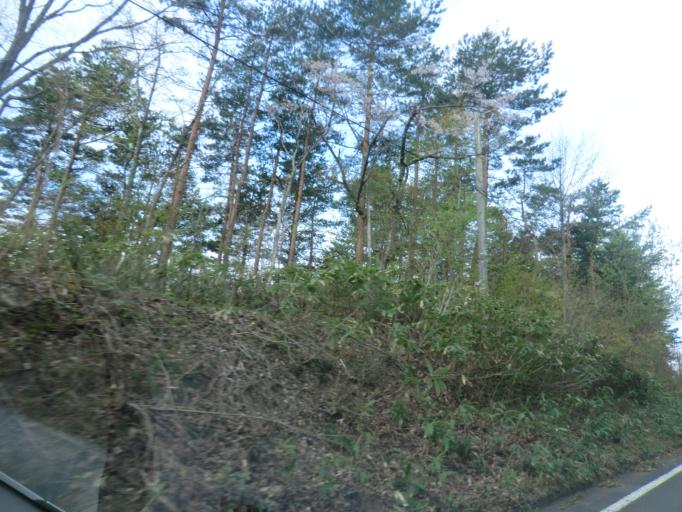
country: JP
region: Aomori
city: Mutsu
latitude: 41.3171
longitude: 141.1513
